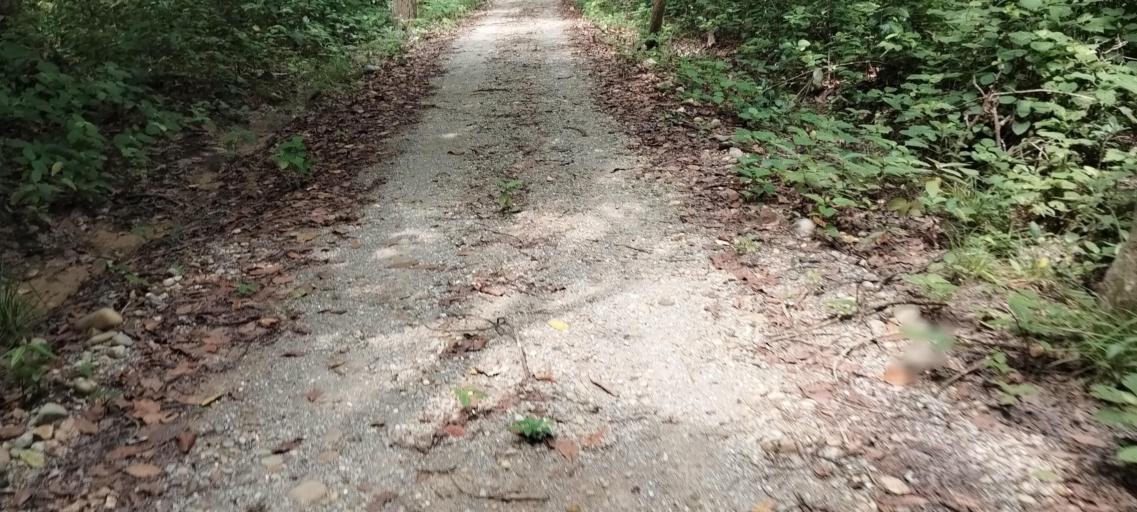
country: NP
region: Far Western
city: Tikapur
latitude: 28.4846
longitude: 81.2523
